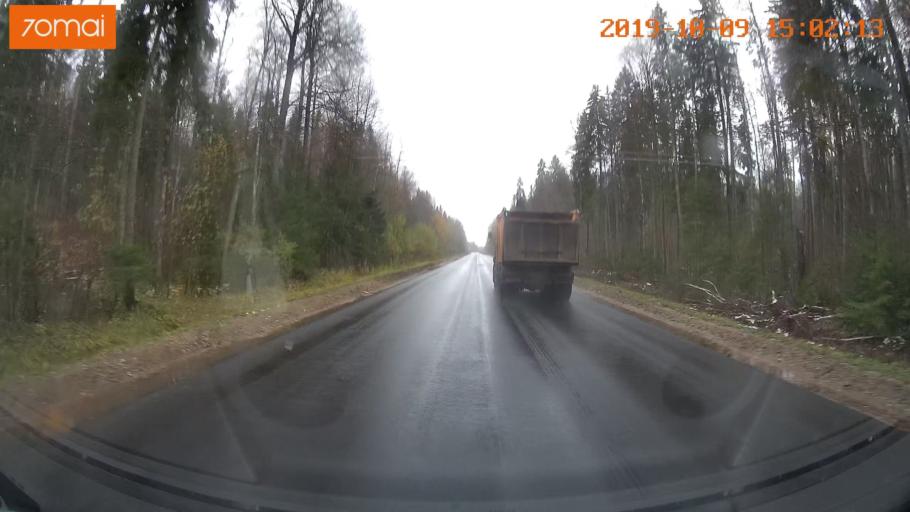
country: RU
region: Kostroma
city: Chistyye Bory
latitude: 58.2883
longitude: 41.6800
